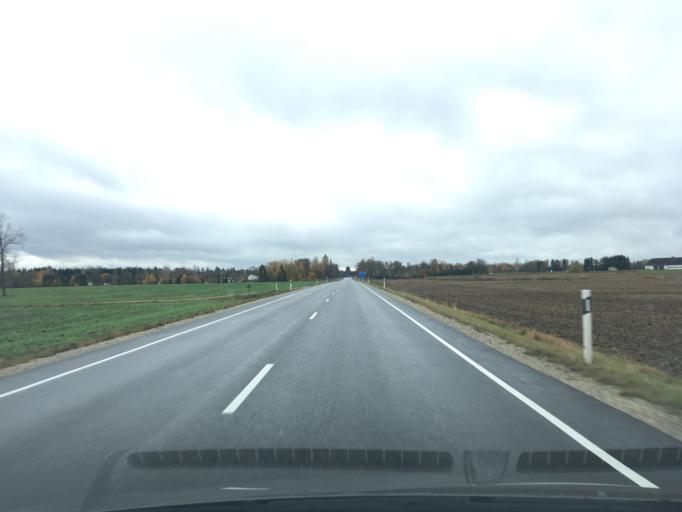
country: EE
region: Jogevamaa
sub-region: Tabivere vald
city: Tabivere
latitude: 58.4352
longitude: 26.4928
